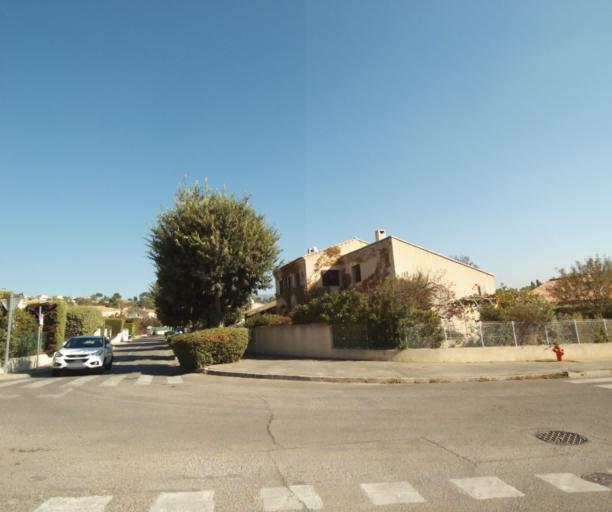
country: FR
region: Provence-Alpes-Cote d'Azur
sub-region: Departement des Bouches-du-Rhone
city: Plan-de-Cuques
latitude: 43.3443
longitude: 5.4545
